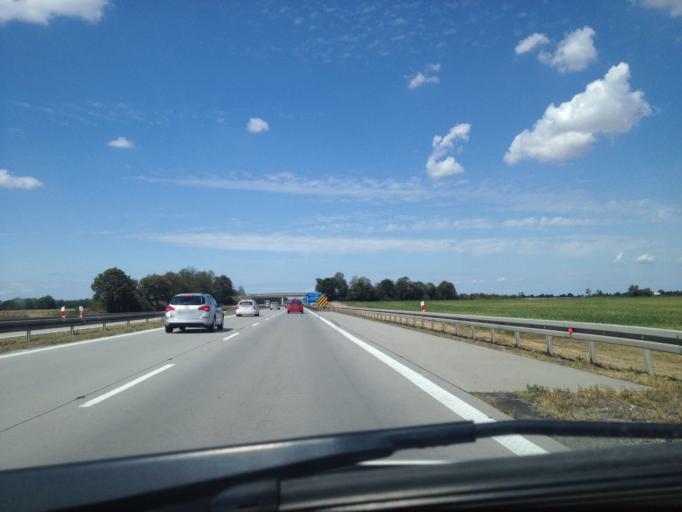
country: PL
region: Lower Silesian Voivodeship
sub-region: Powiat sredzki
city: Ciechow
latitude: 51.0562
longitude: 16.5372
